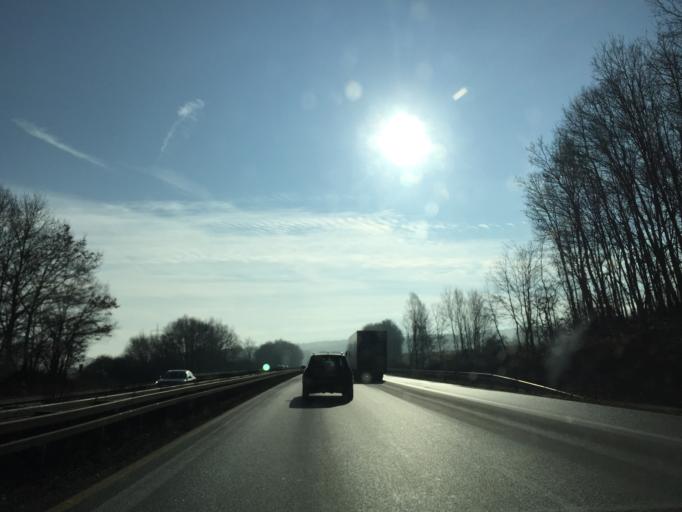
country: DE
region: Bavaria
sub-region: Upper Franconia
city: Schlusselfeld
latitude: 49.7381
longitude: 10.6559
